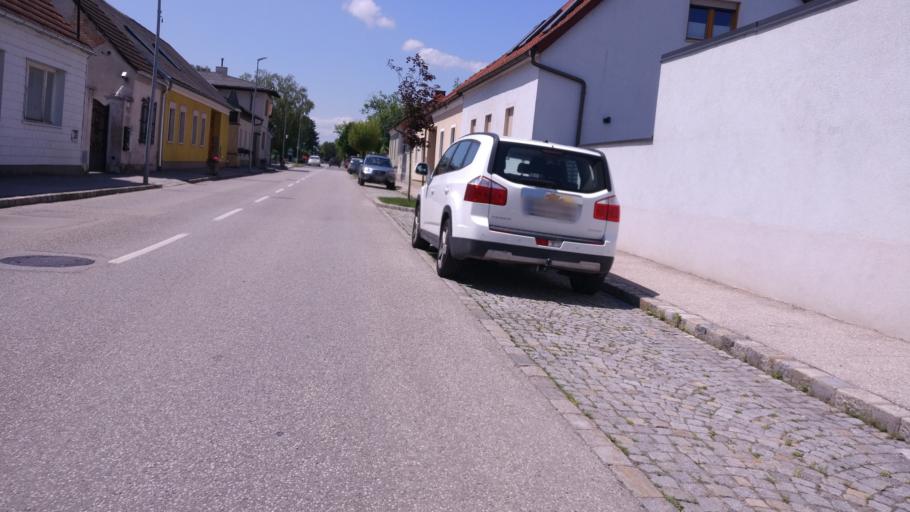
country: AT
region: Lower Austria
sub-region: Politischer Bezirk Baden
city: Schonau an der Triesting
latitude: 47.9335
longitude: 16.2544
